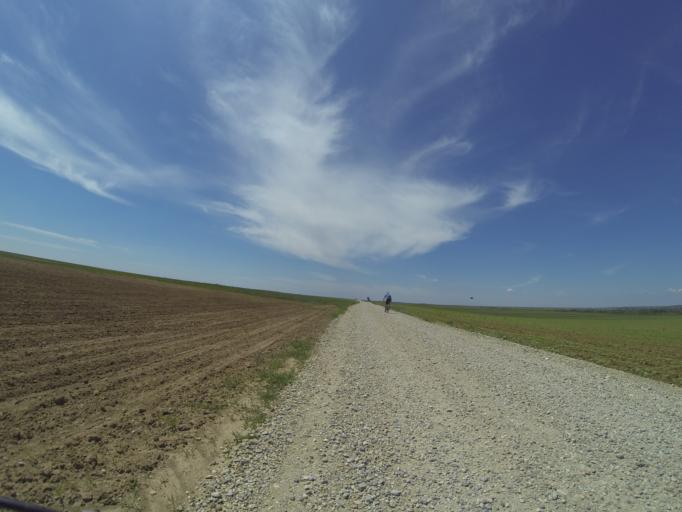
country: RO
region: Dolj
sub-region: Comuna Teslui
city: Teslui
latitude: 44.1893
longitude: 24.1653
